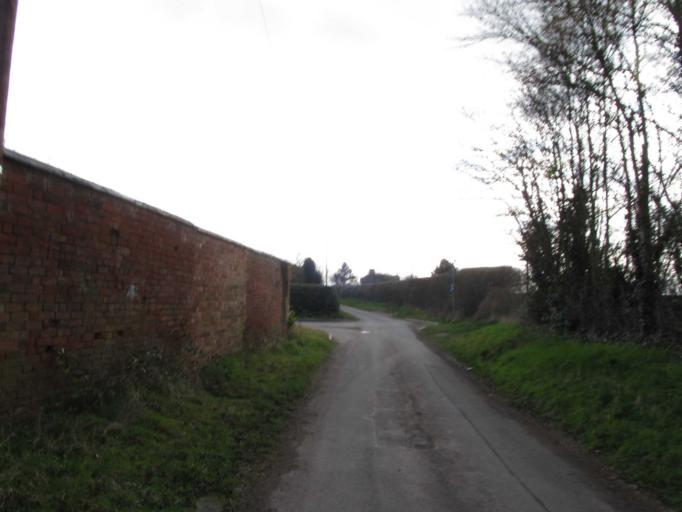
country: GB
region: England
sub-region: Leicestershire
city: Barrow upon Soar
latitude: 52.7961
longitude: -1.1482
